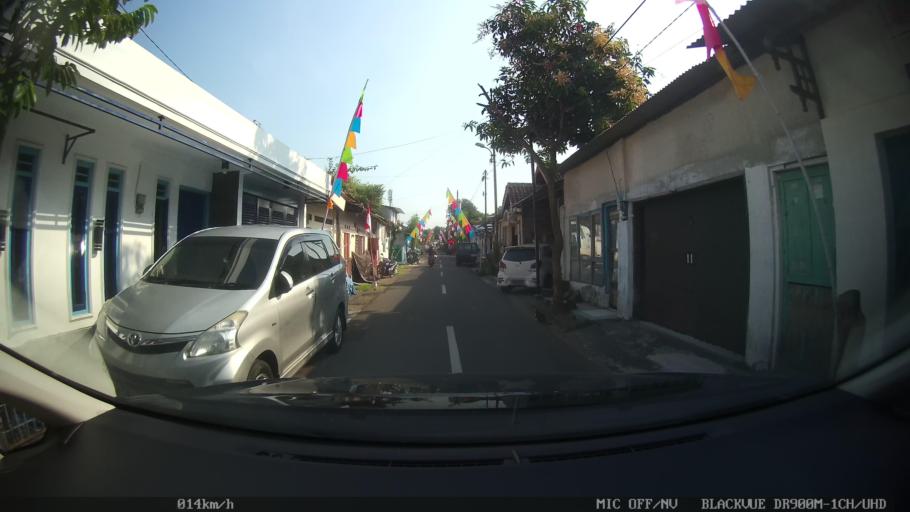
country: ID
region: Daerah Istimewa Yogyakarta
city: Yogyakarta
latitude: -7.8069
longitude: 110.3564
